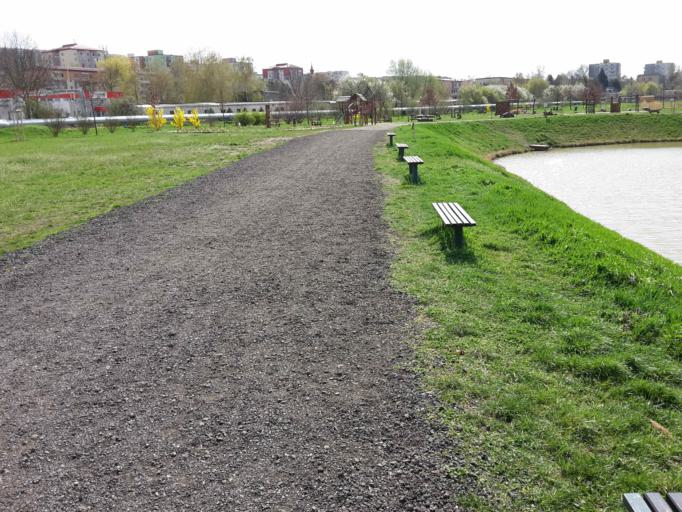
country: SK
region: Trnavsky
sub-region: Okres Skalica
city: Holic
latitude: 48.8087
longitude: 17.1589
